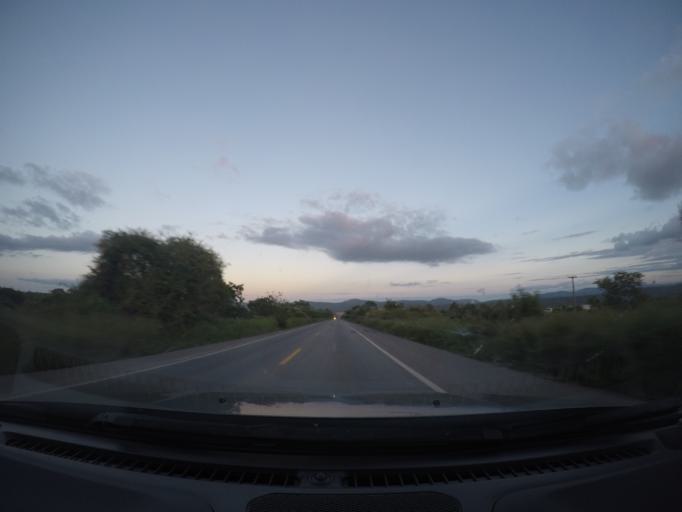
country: BR
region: Bahia
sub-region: Seabra
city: Seabra
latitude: -12.4307
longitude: -41.7951
